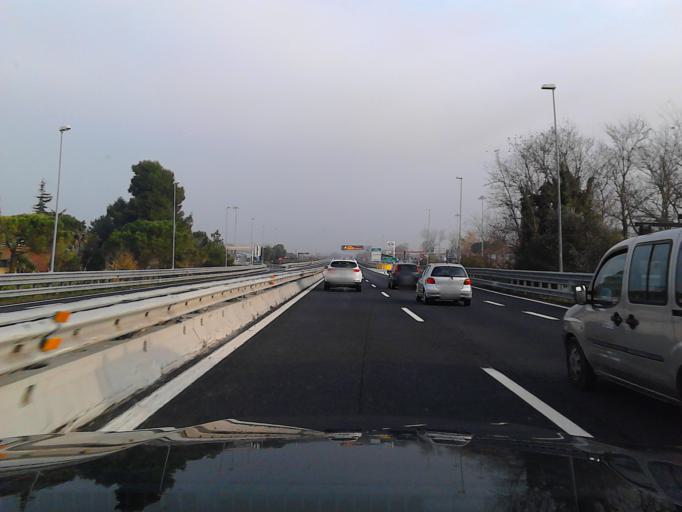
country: IT
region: Abruzzo
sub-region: Provincia di Pescara
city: San Martino Bassa
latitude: 42.5319
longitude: 14.1216
